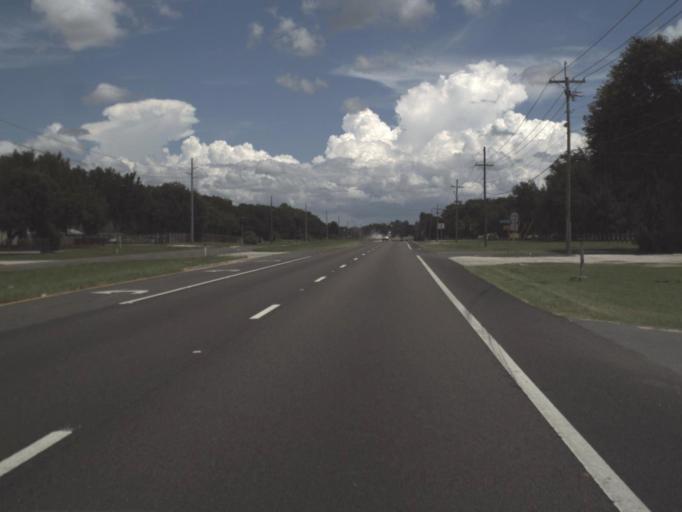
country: US
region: Florida
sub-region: Polk County
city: Bartow
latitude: 27.9058
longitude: -81.8049
